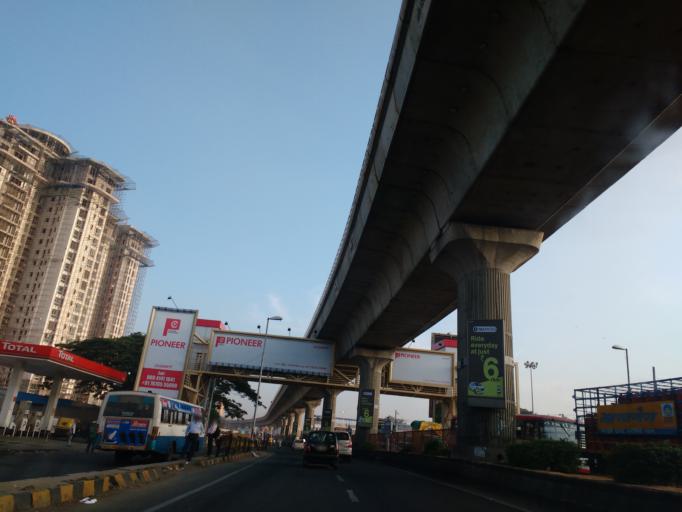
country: IN
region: Karnataka
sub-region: Bangalore Urban
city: Bangalore
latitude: 13.0192
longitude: 77.5530
